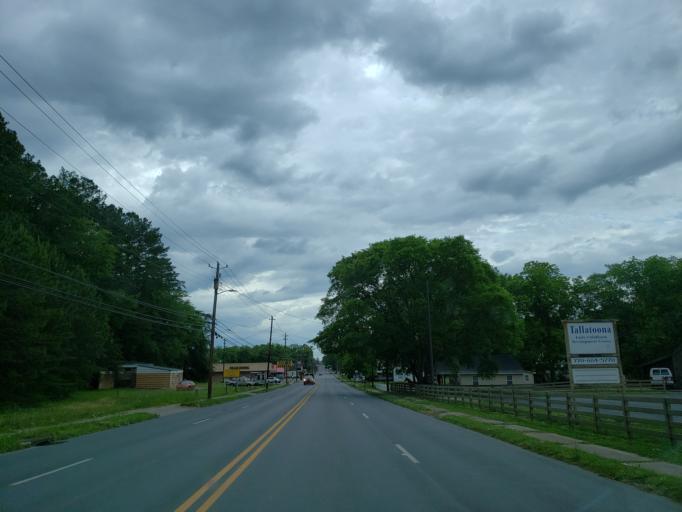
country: US
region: Georgia
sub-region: Polk County
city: Rockmart
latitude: 33.9931
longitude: -85.0415
